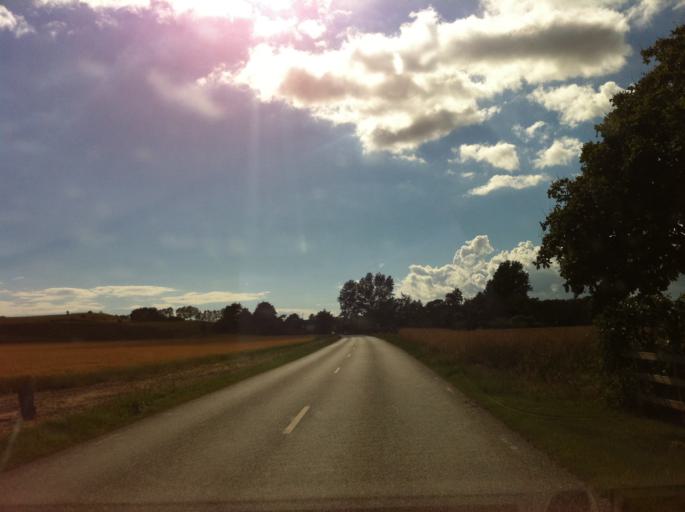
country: SE
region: Skane
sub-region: Ystads Kommun
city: Kopingebro
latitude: 55.3961
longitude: 14.0358
